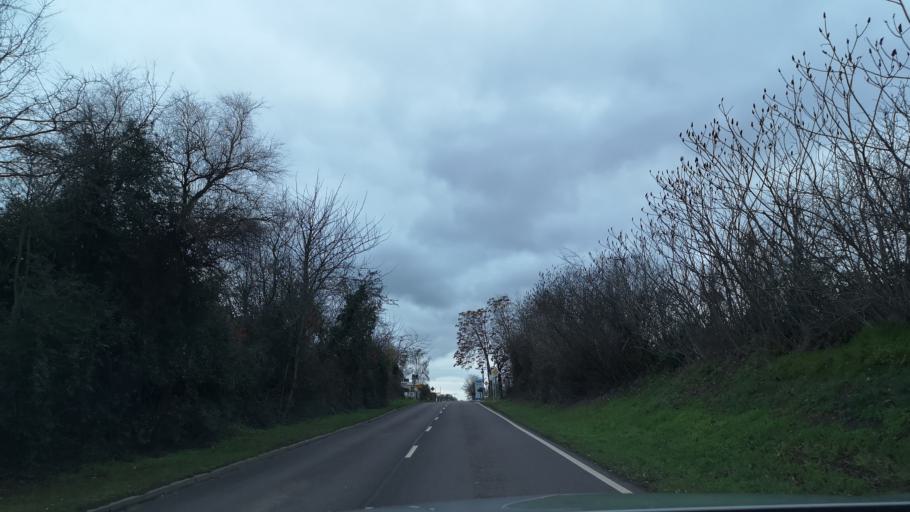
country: DE
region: Saxony-Anhalt
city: Mucheln
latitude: 51.2965
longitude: 11.8030
